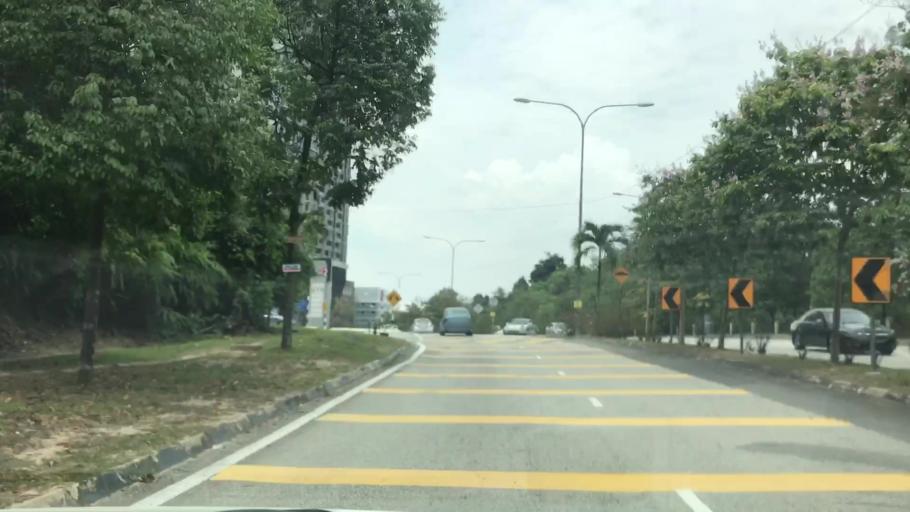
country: MY
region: Selangor
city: Kampong Baharu Balakong
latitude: 3.0528
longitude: 101.6775
